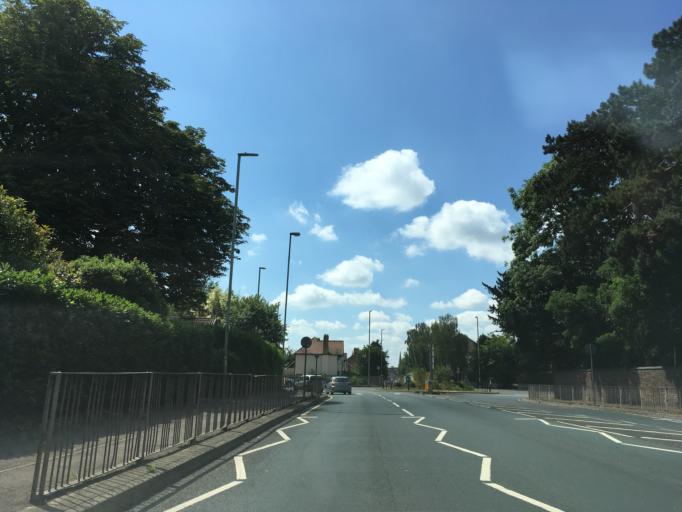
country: GB
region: England
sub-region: Gloucestershire
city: Gloucester
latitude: 51.8766
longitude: -2.2405
